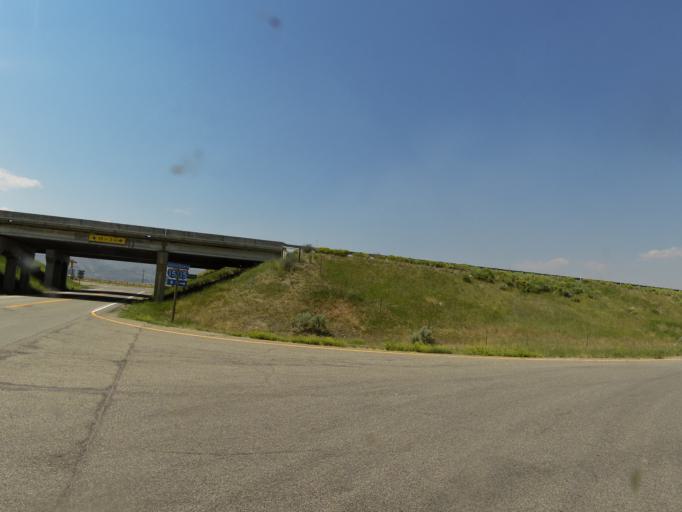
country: US
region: Idaho
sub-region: Clark County
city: Dubois
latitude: 44.6324
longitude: -112.5922
